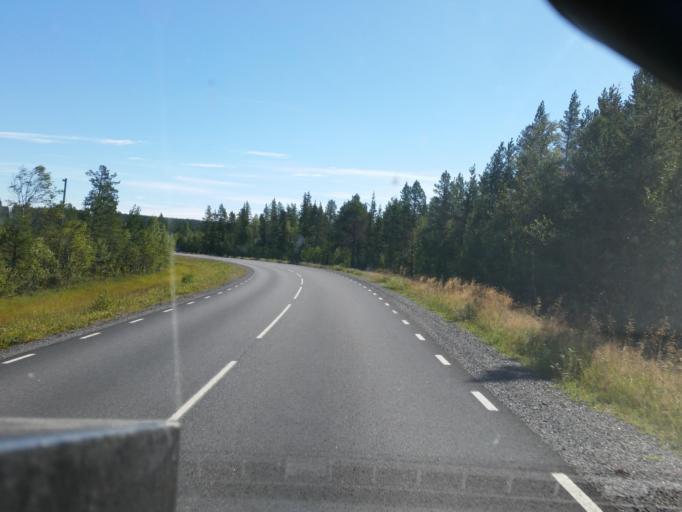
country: SE
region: Vaesterbotten
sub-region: Skelleftea Kommun
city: Storvik
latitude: 65.3252
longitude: 20.6950
